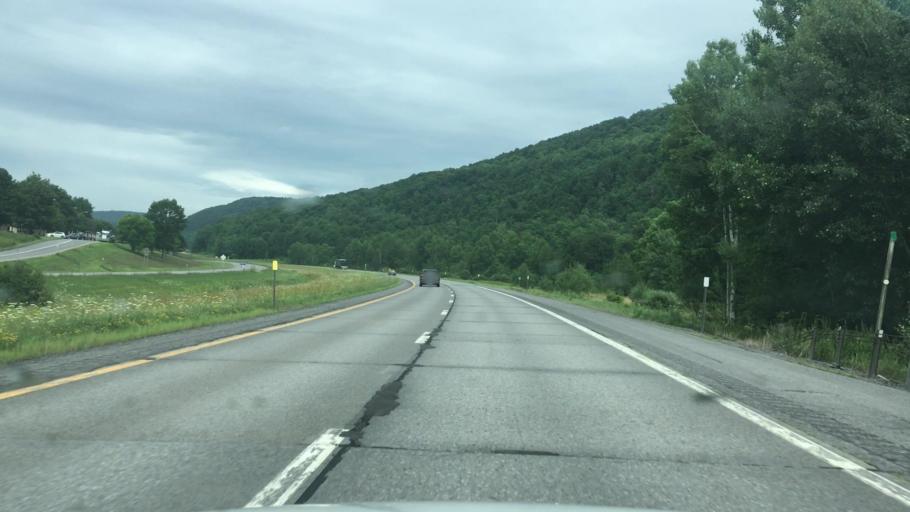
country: US
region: New York
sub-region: Otsego County
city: Worcester
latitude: 42.6068
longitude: -74.6882
